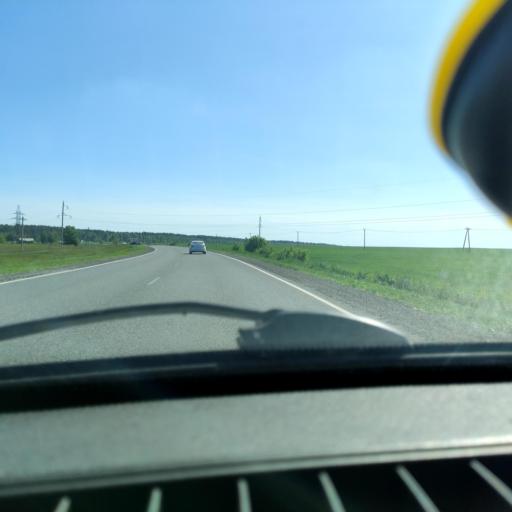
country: RU
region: Samara
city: Povolzhskiy
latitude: 53.6382
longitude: 49.6592
